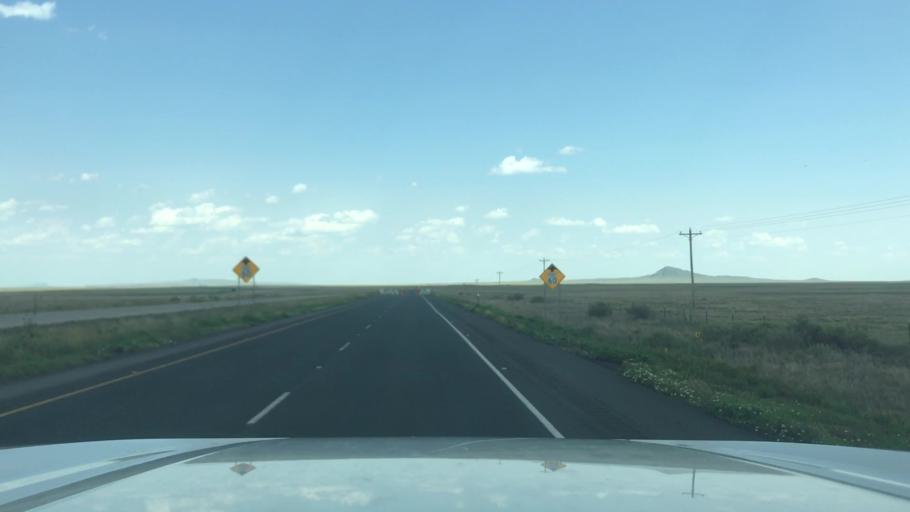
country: US
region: New Mexico
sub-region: Union County
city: Clayton
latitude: 36.6228
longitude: -103.6993
